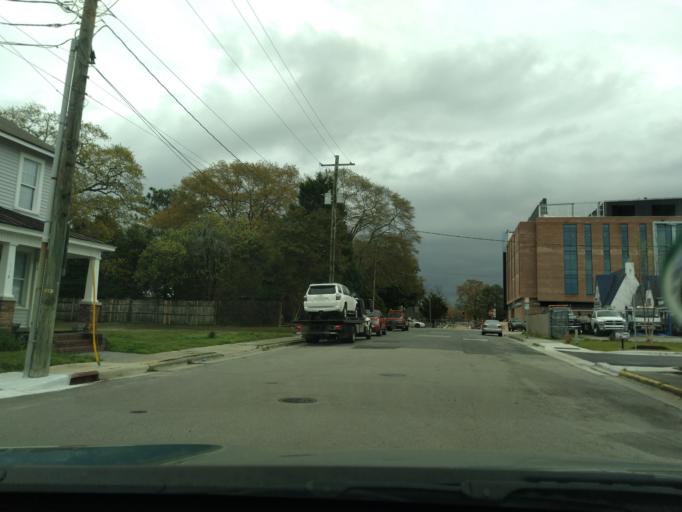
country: US
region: North Carolina
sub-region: Pitt County
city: Greenville
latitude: 35.6072
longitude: -77.3751
